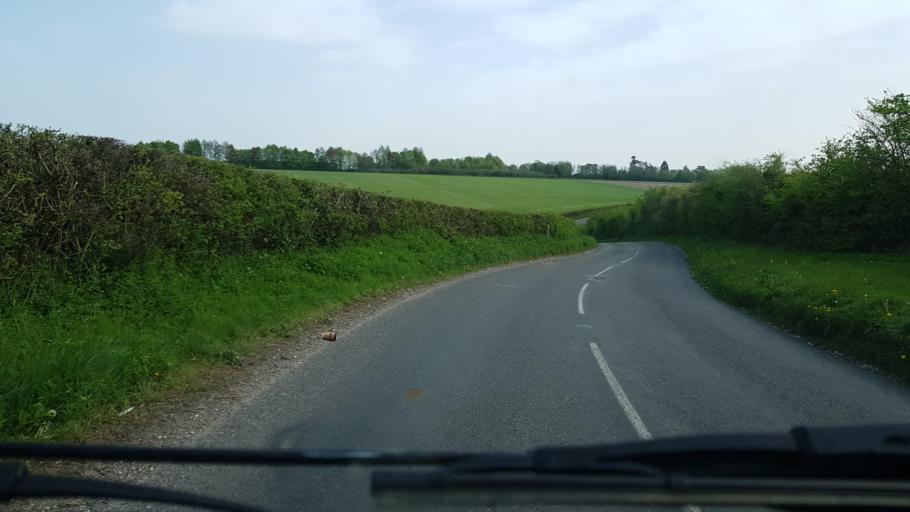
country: GB
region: England
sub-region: Hampshire
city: Overton
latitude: 51.2593
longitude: -1.2639
